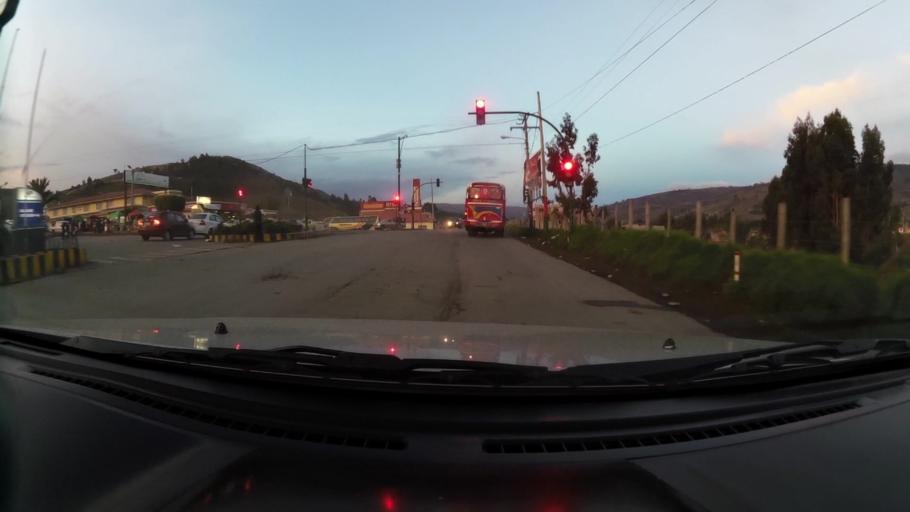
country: EC
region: Chimborazo
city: Riobamba
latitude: -1.9351
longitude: -78.7072
